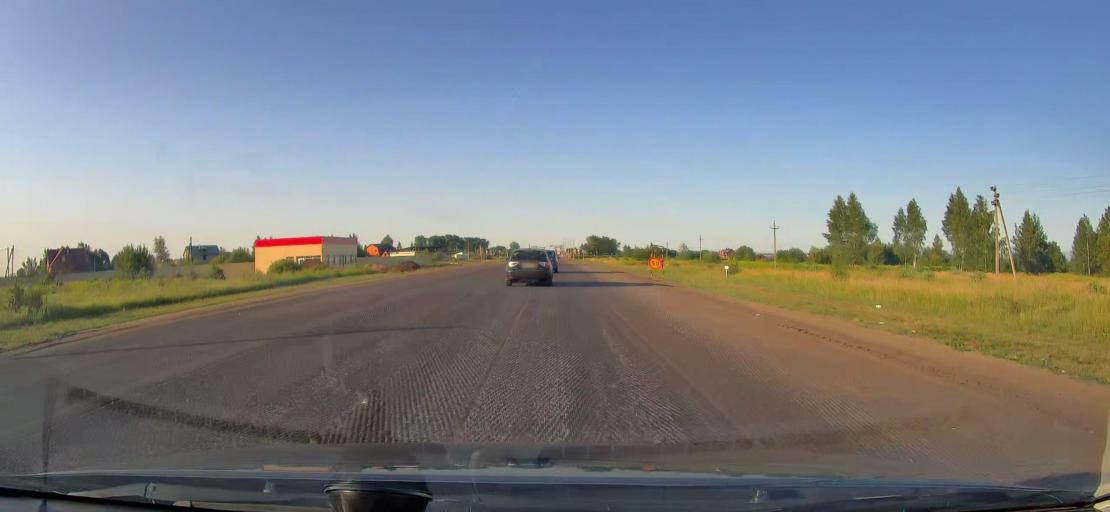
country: RU
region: Tula
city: Shchekino
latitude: 54.0006
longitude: 37.4749
